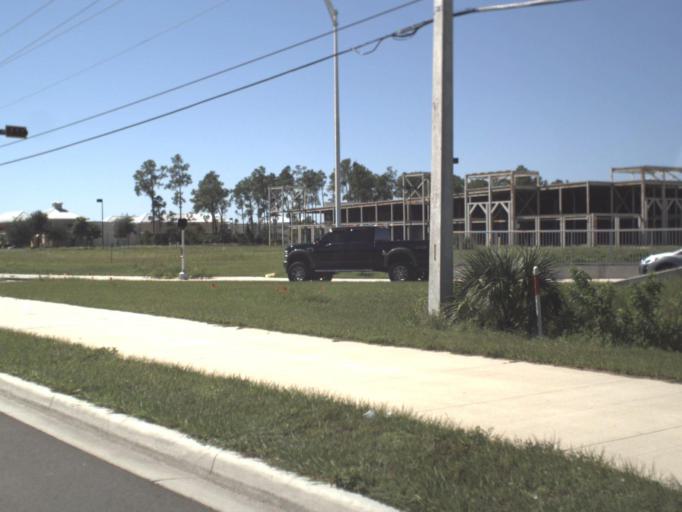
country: US
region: Florida
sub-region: Collier County
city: Golden Gate
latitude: 26.1539
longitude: -81.6866
